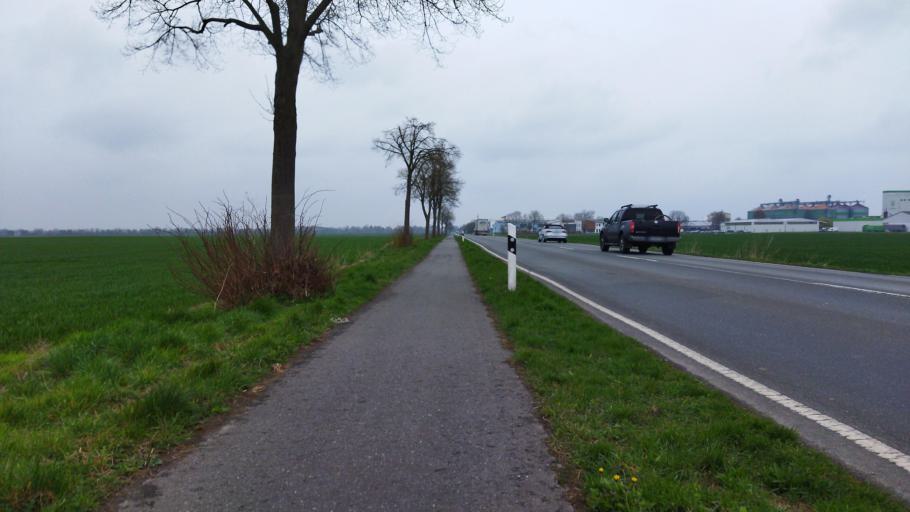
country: DE
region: Lower Saxony
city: Schweringen
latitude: 52.7327
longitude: 9.1866
